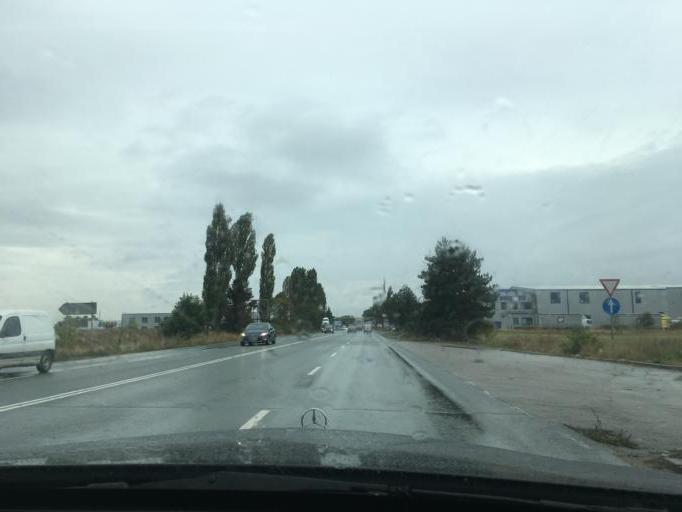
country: BG
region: Sofiya
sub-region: Obshtina Bozhurishte
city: Bozhurishte
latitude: 42.7399
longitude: 23.2384
